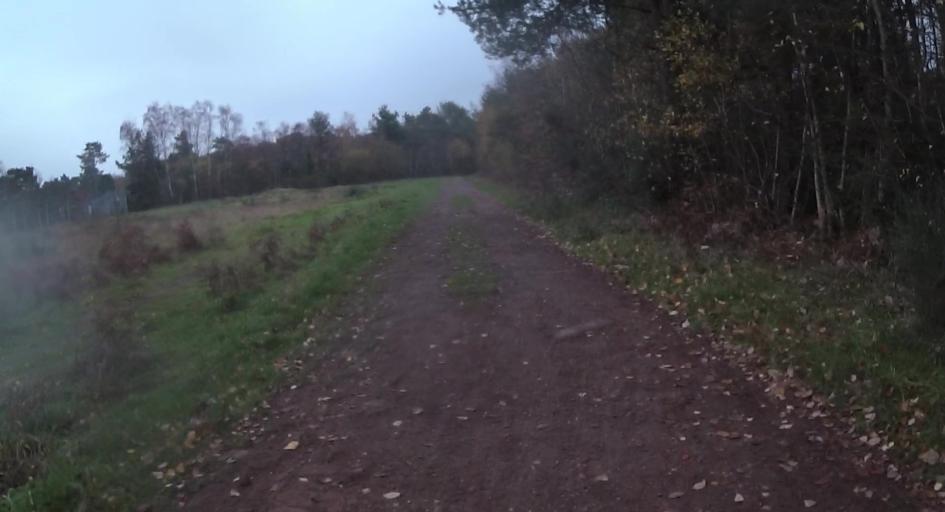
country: GB
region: England
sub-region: Surrey
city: Bagshot
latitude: 51.3234
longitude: -0.6951
